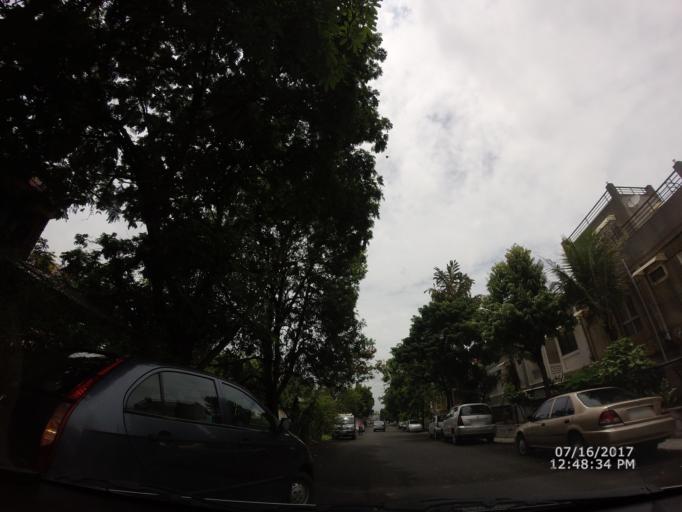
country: IN
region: Gujarat
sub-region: Ahmadabad
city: Sarkhej
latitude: 23.0180
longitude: 72.5095
